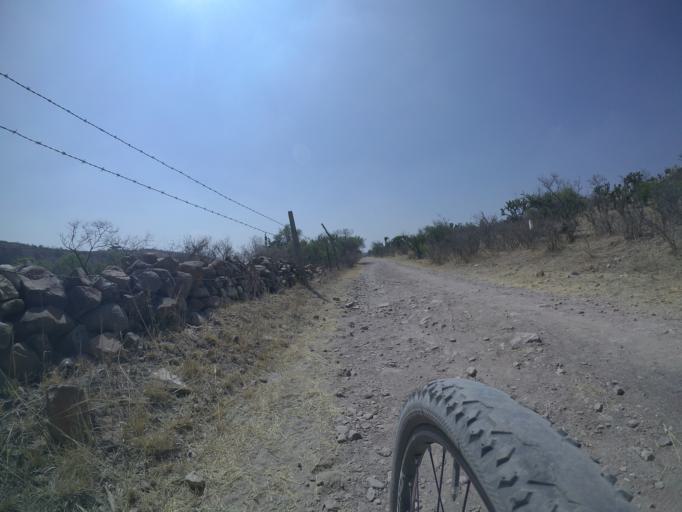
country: MX
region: Aguascalientes
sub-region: Jesus Maria
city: Paseos de las Haciendas [Fraccionamiento]
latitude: 22.0053
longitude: -102.3712
